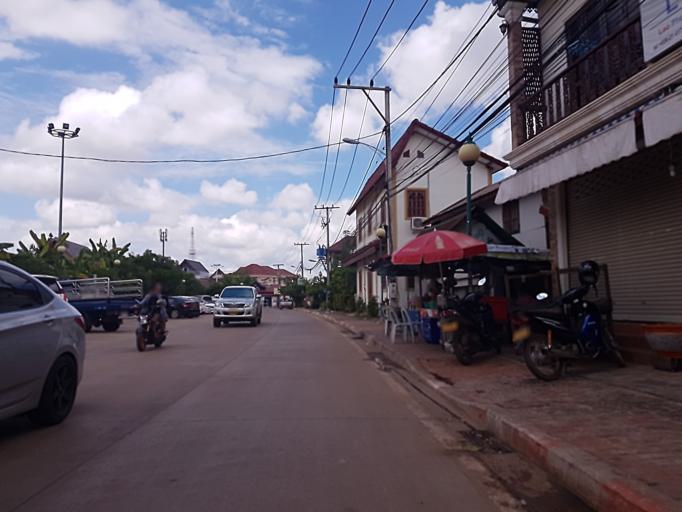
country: LA
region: Vientiane
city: Vientiane
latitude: 17.9777
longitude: 102.6372
